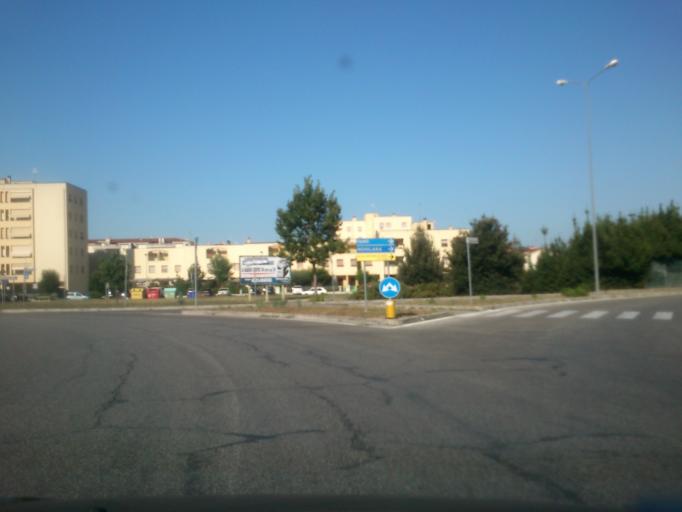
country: IT
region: The Marches
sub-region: Provincia di Pesaro e Urbino
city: Pesaro
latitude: 43.8889
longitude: 12.9002
